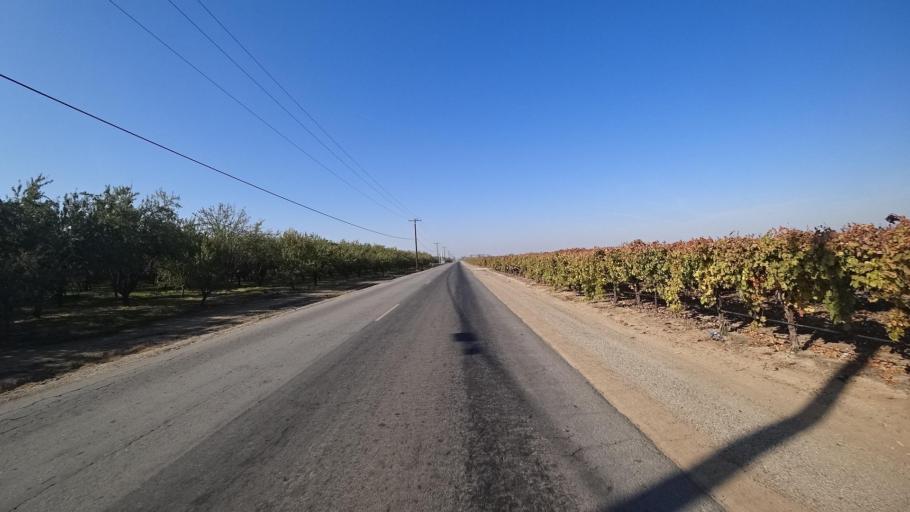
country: US
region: California
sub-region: Kern County
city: McFarland
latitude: 35.7179
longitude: -119.2109
